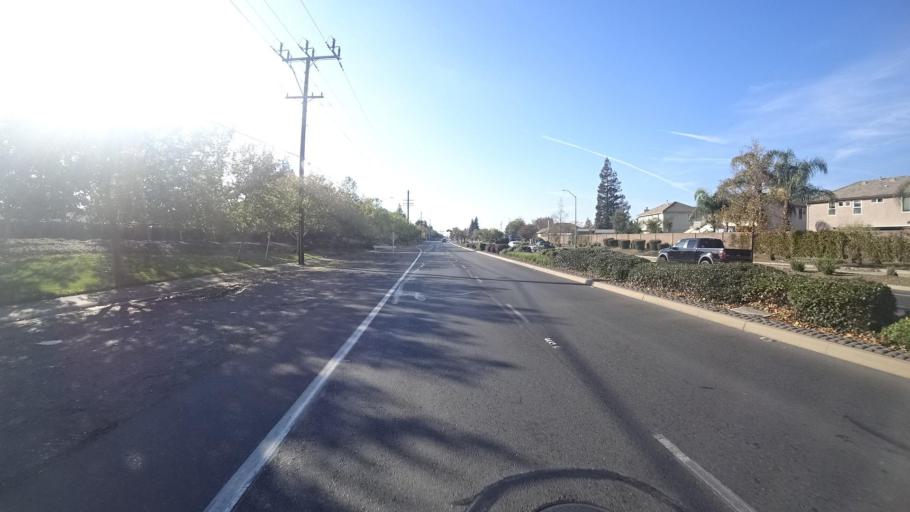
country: US
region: California
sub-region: Sacramento County
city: Vineyard
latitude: 38.4525
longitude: -121.3825
